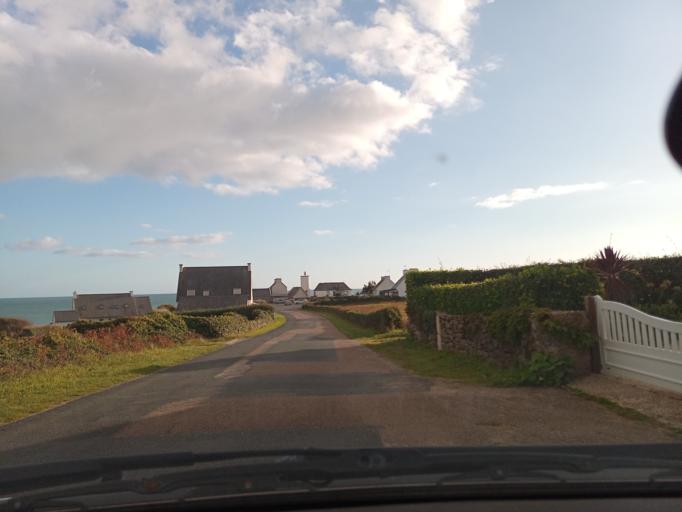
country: FR
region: Brittany
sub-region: Departement du Finistere
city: Esquibien
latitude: 48.0028
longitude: -4.5653
